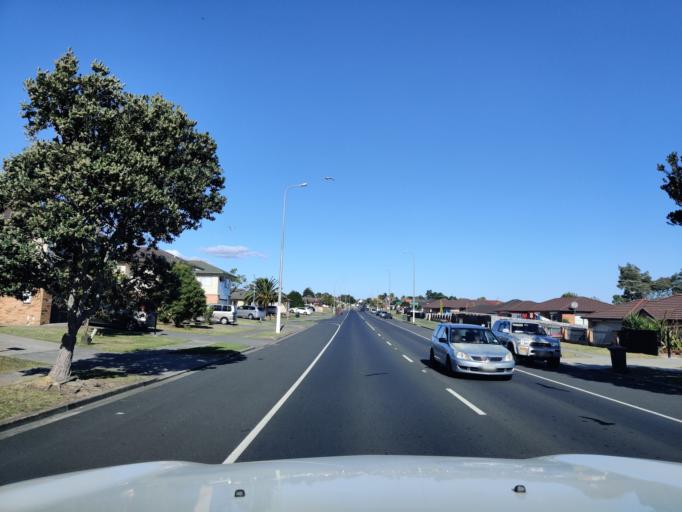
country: NZ
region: Auckland
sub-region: Auckland
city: Takanini
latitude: -37.0373
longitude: 174.8739
